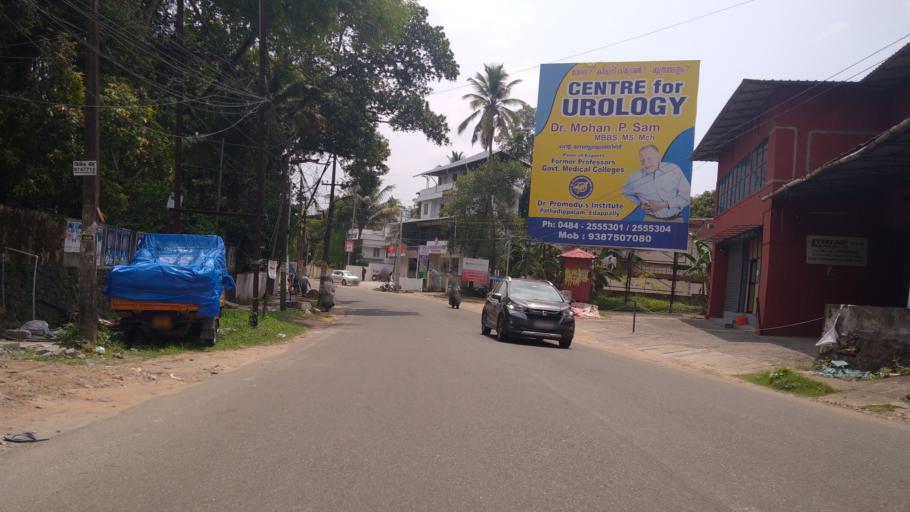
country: IN
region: Kerala
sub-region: Ernakulam
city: Elur
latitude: 10.0280
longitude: 76.3163
